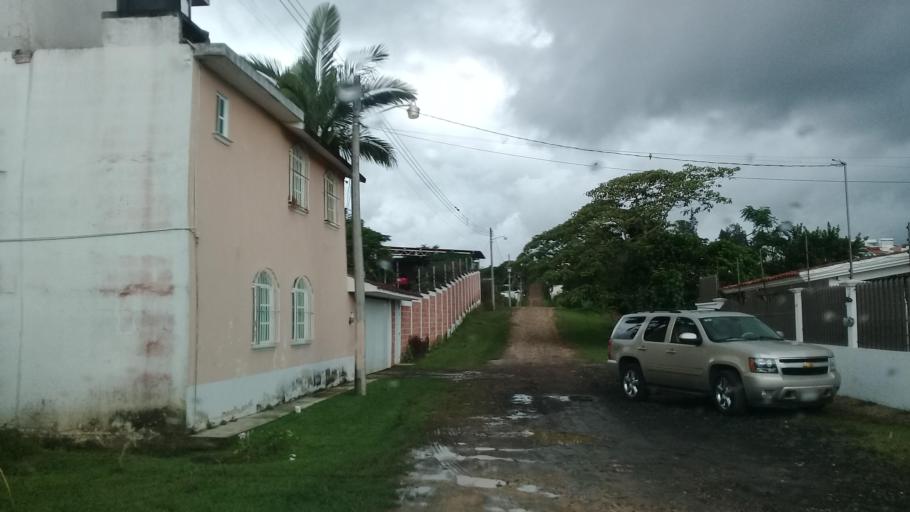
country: MX
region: Veracruz
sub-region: Emiliano Zapata
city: Jacarandas
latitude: 19.5096
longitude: -96.8490
